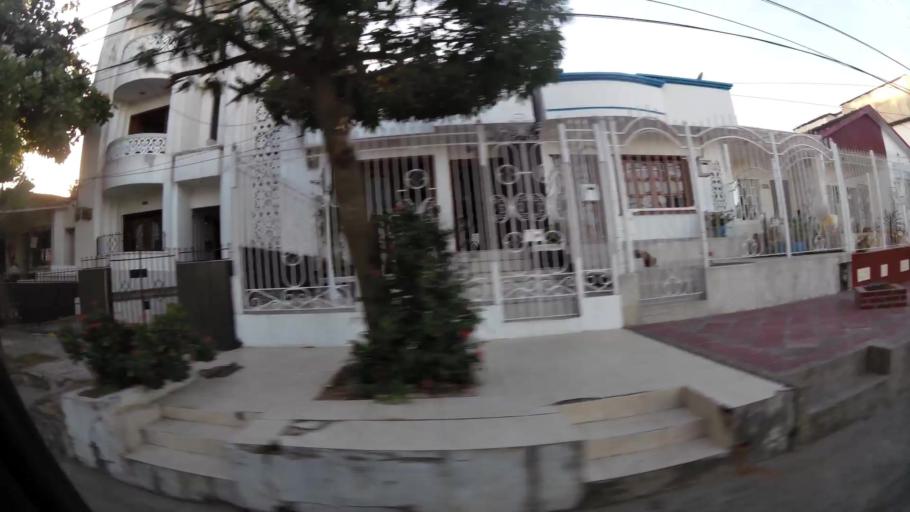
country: CO
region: Atlantico
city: Barranquilla
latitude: 10.9782
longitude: -74.8051
